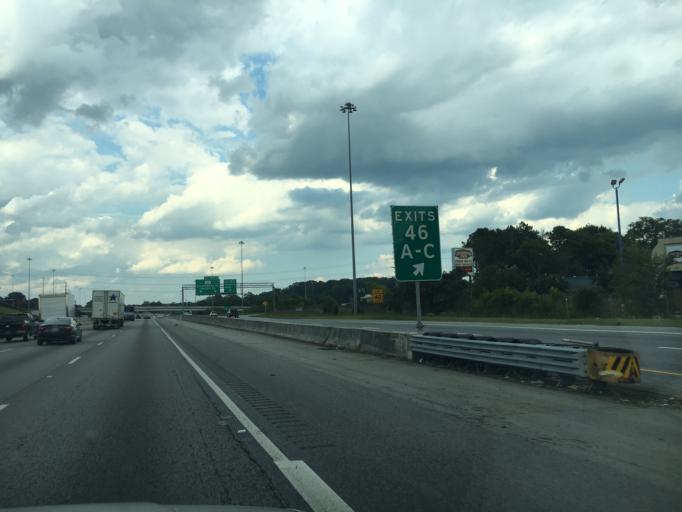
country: US
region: South Carolina
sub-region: Greenville County
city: Gantt
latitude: 34.7951
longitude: -82.3853
